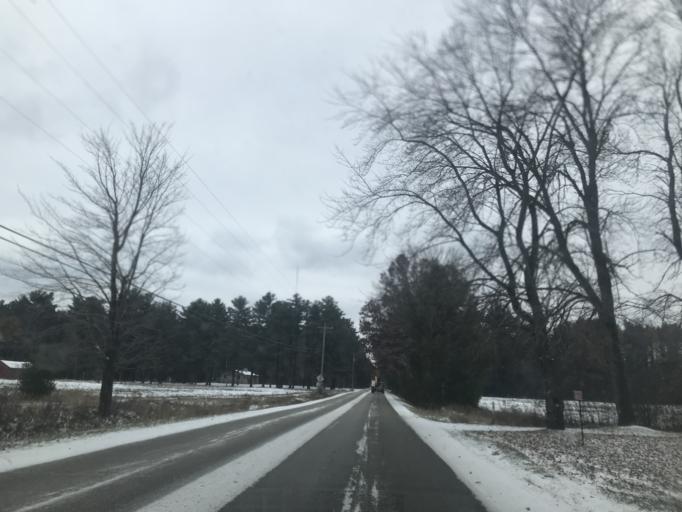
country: US
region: Wisconsin
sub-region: Marinette County
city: Marinette
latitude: 45.0692
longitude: -87.6595
